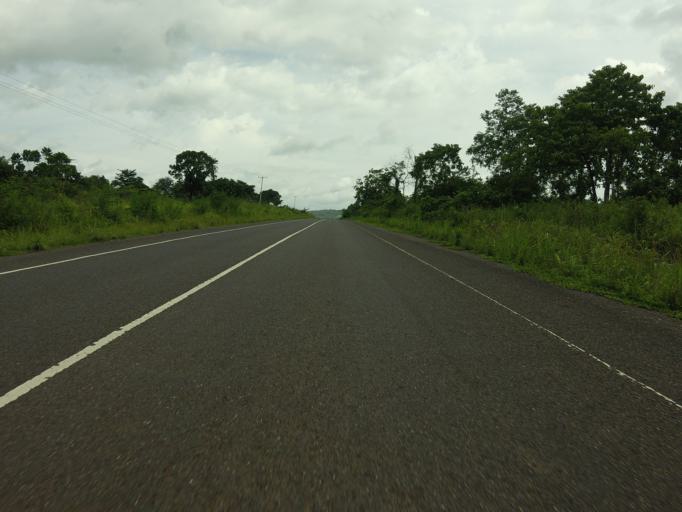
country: TG
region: Plateaux
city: Badou
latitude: 7.9684
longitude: 0.5578
